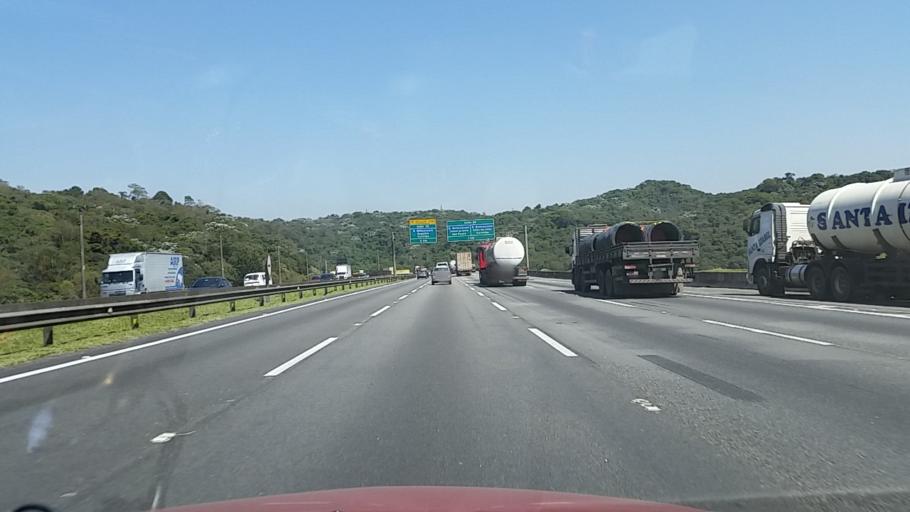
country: BR
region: Sao Paulo
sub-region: Taboao Da Serra
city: Taboao da Serra
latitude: -23.6158
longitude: -46.8244
